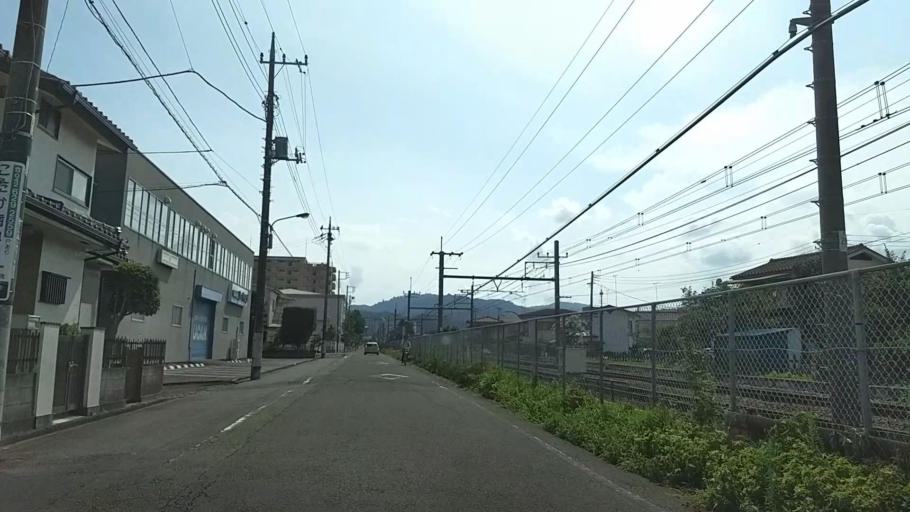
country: JP
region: Tokyo
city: Hachioji
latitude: 35.6497
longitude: 139.2999
